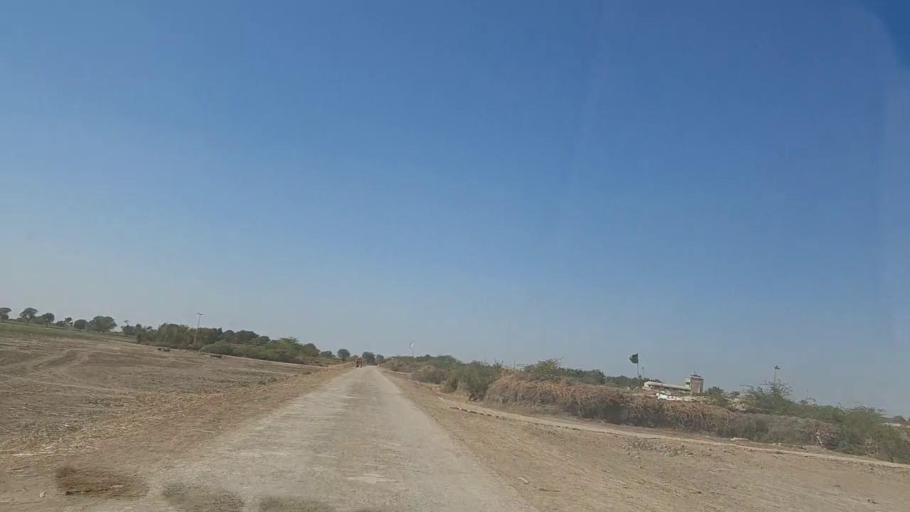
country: PK
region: Sindh
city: Digri
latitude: 25.1235
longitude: 69.0751
